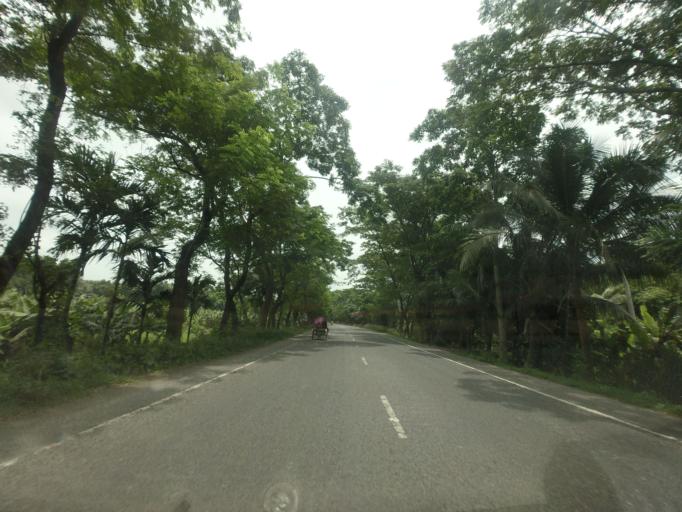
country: BD
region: Khulna
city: Kalia
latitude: 23.2212
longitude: 89.7276
